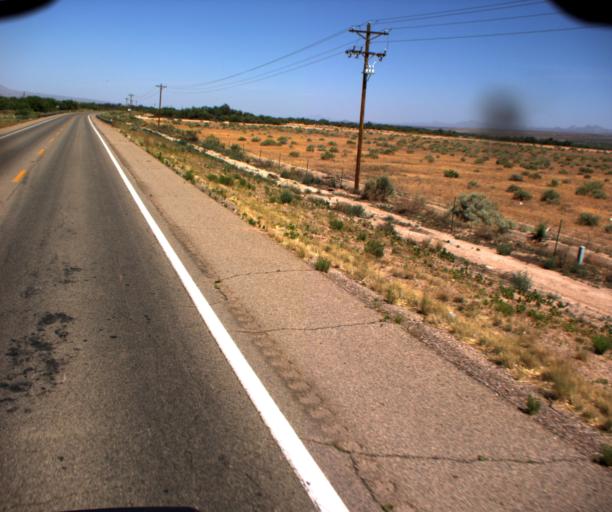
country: US
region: Arizona
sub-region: Graham County
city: Bylas
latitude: 33.0399
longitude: -109.9734
